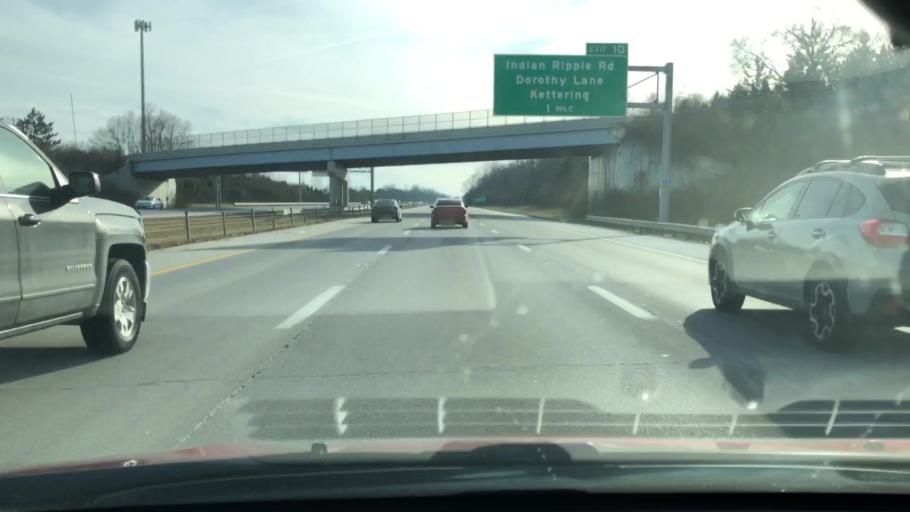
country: US
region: Ohio
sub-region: Greene County
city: Beavercreek
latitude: 39.7160
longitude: -84.0919
